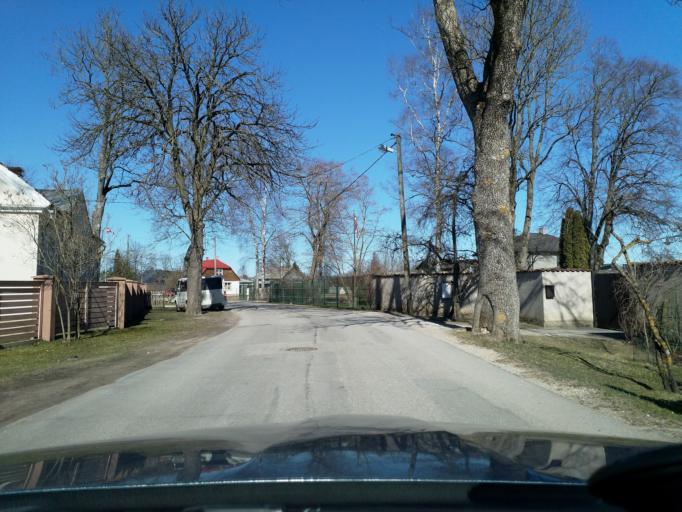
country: LV
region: Kuldigas Rajons
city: Kuldiga
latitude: 56.9649
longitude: 21.9987
